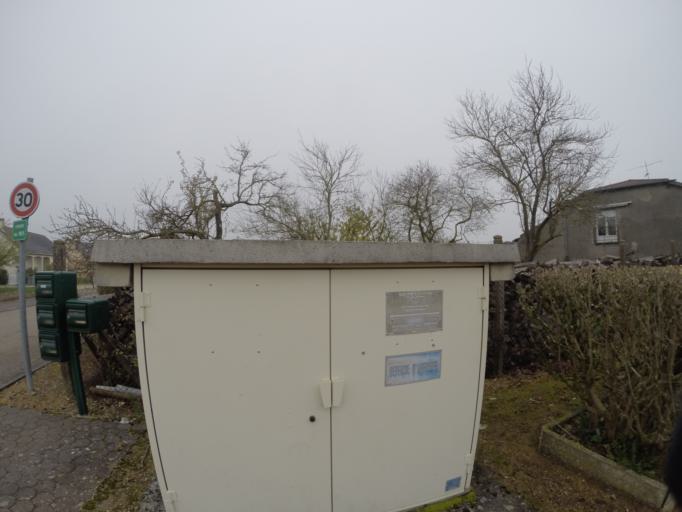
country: FR
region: Lorraine
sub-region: Departement de Meurthe-et-Moselle
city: Colombey-les-Belles
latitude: 48.5252
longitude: 5.8393
